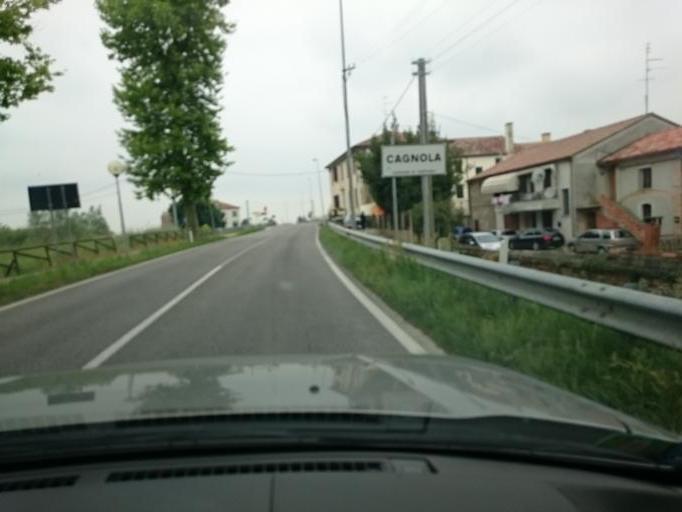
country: IT
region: Veneto
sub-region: Provincia di Padova
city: Cartura
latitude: 45.2867
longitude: 11.8707
